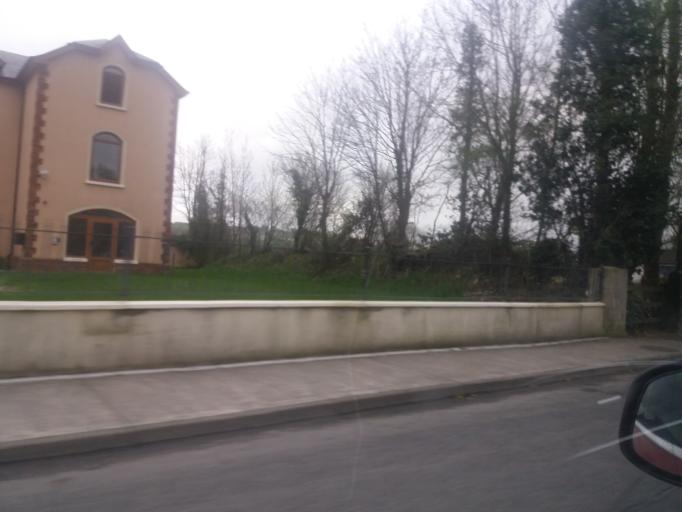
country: IE
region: Munster
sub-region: County Limerick
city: Abbeyfeale
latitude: 52.3880
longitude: -9.2877
